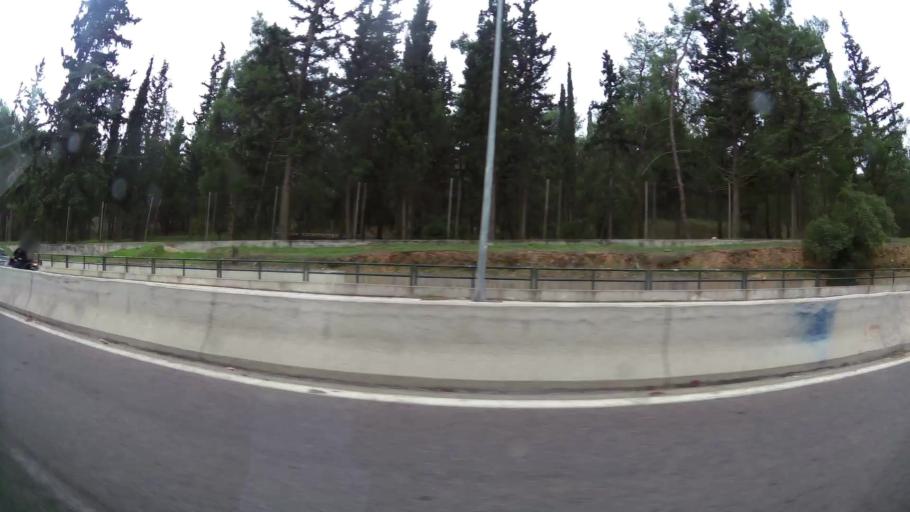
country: GR
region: Attica
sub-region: Nomarchia Athinas
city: Chaidari
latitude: 38.0051
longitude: 23.6538
